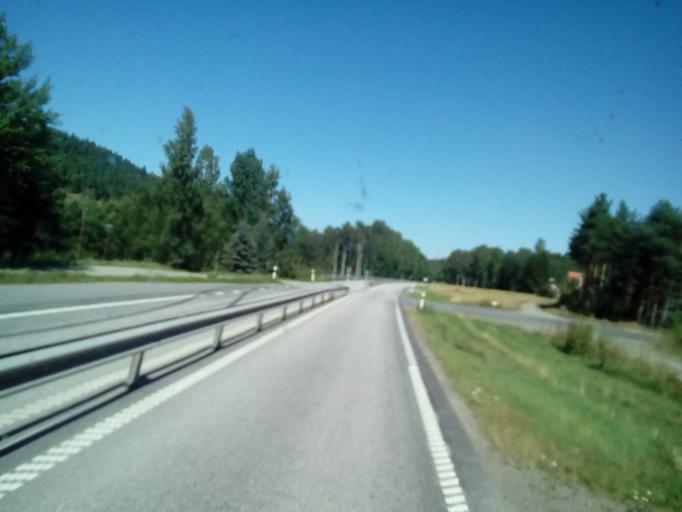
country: SE
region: OEstergoetland
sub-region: Kinda Kommun
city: Kisa
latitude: 58.0294
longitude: 15.6578
